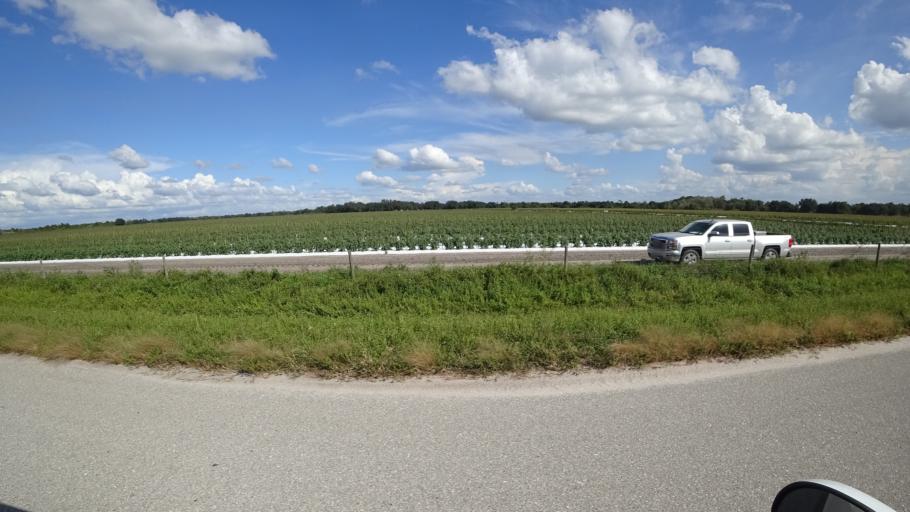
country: US
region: Florida
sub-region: DeSoto County
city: Arcadia
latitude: 27.2762
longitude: -82.0562
